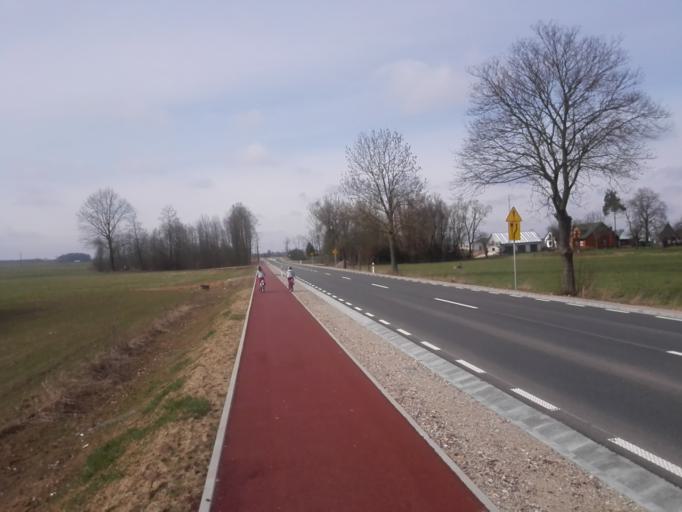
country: PL
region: Podlasie
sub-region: Powiat sejnenski
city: Sejny
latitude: 54.1098
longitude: 23.3241
